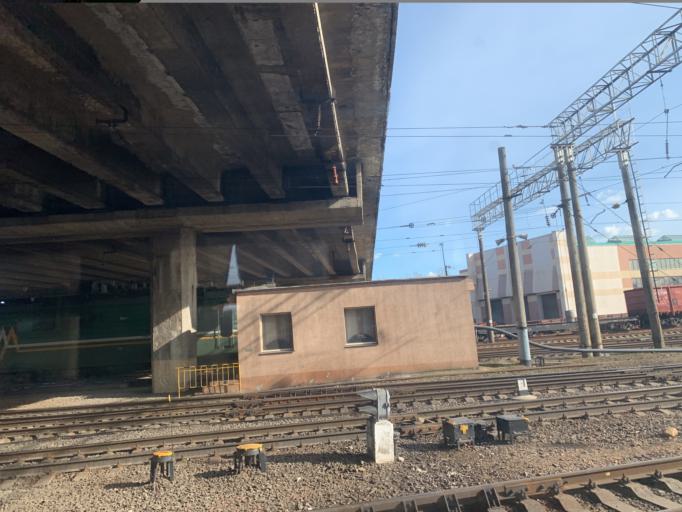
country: BY
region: Minsk
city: Syenitsa
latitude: 53.8757
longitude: 27.5221
